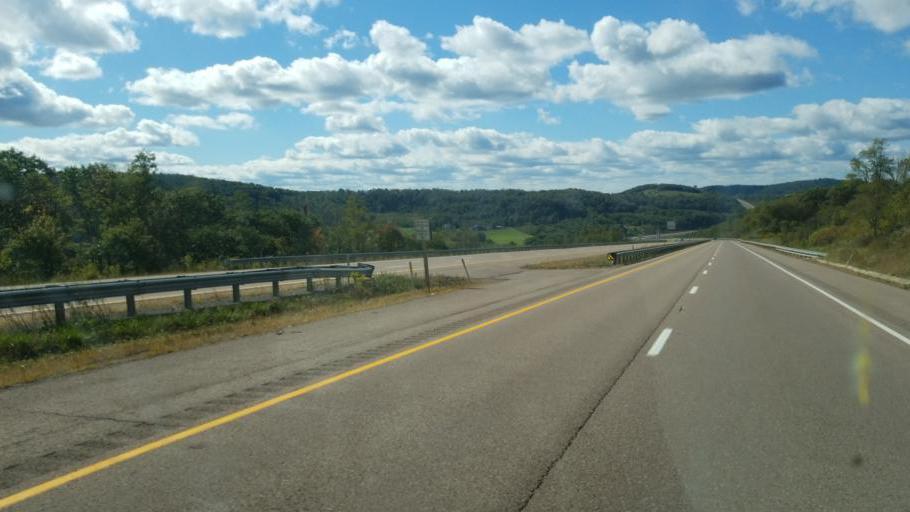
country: US
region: Pennsylvania
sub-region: Somerset County
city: Meyersdale
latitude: 39.6945
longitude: -79.2606
